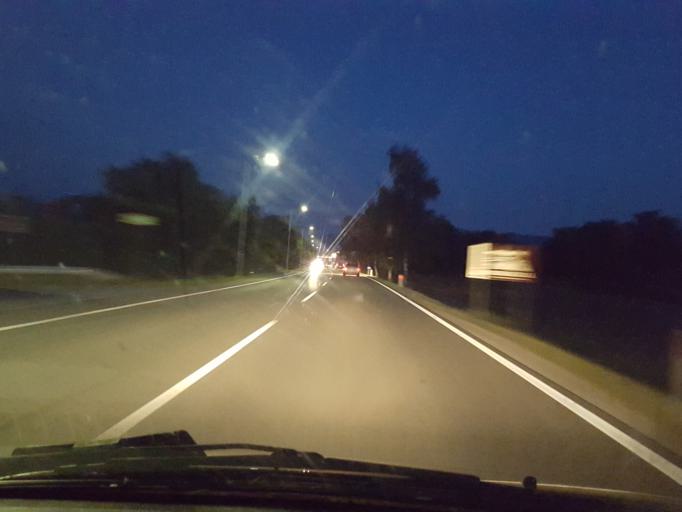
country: AT
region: Lower Austria
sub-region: Politischer Bezirk Scheibbs
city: Purgstall
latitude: 48.0756
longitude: 15.1369
